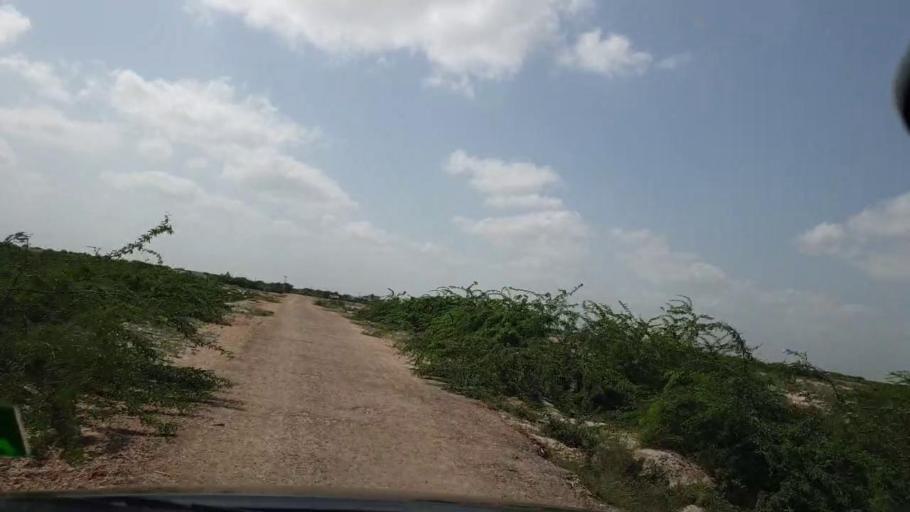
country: PK
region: Sindh
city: Kadhan
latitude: 24.5901
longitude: 69.1593
